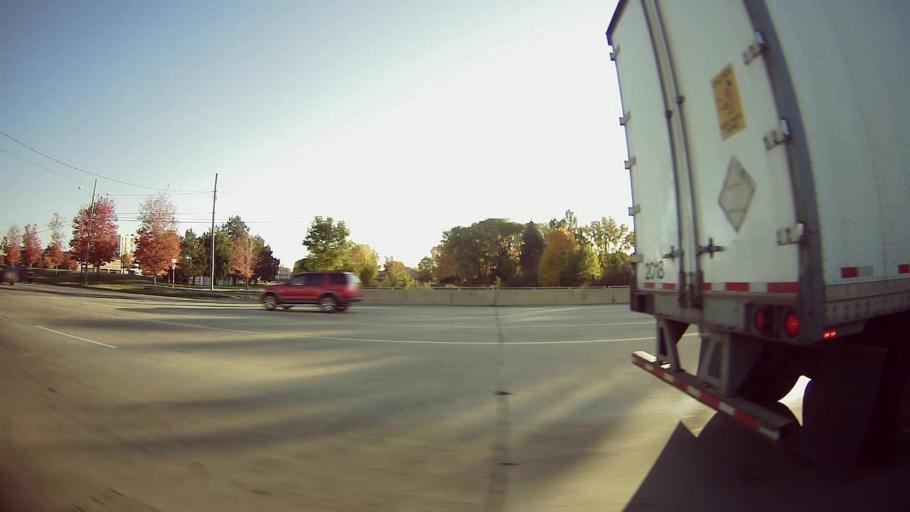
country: US
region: Michigan
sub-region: Macomb County
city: Center Line
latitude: 42.5259
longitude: -83.0292
